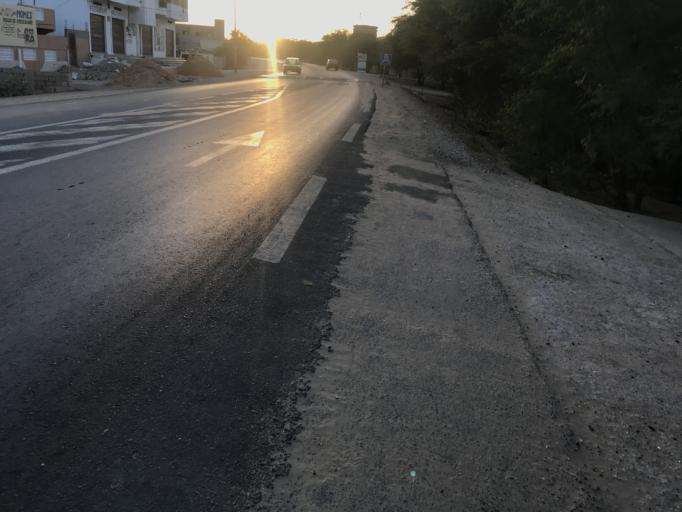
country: SN
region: Saint-Louis
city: Saint-Louis
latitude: 16.0608
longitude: -16.4181
